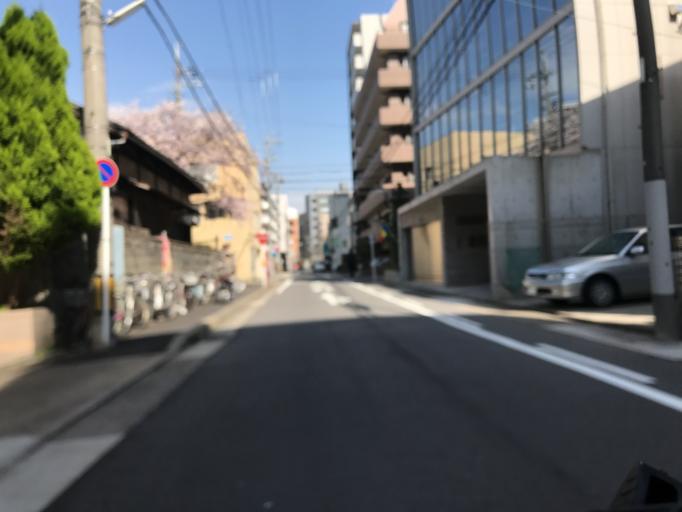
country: JP
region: Aichi
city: Nagoya-shi
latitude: 35.1712
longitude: 136.9342
